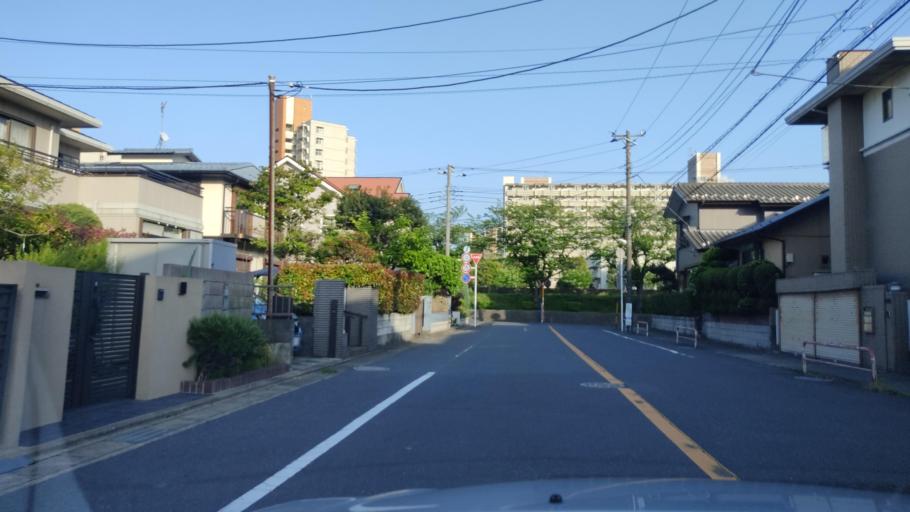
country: JP
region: Tokyo
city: Urayasu
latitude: 35.6642
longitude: 139.9075
